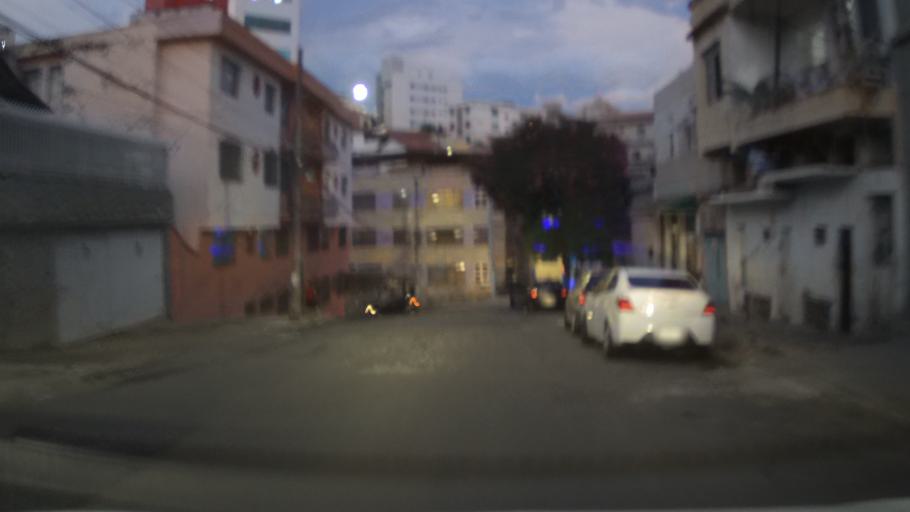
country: BR
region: Minas Gerais
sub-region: Belo Horizonte
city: Belo Horizonte
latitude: -19.9014
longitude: -43.9339
